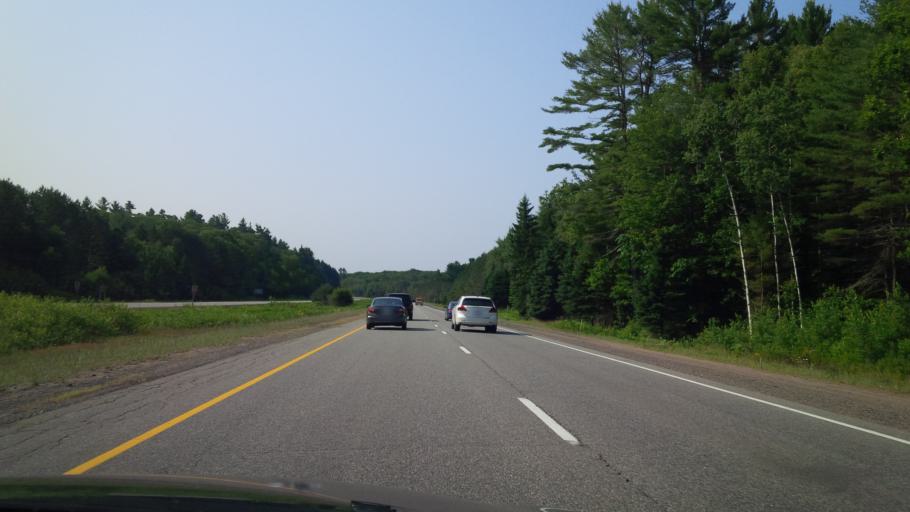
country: CA
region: Ontario
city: Bracebridge
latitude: 45.1119
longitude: -79.3109
